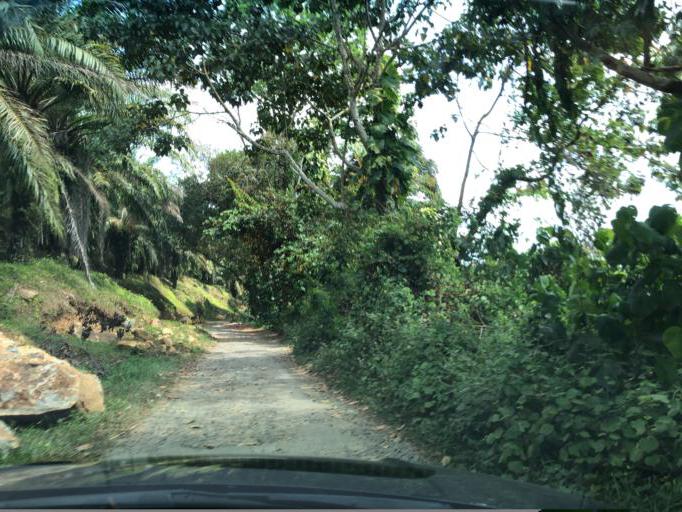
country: LK
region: Western
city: Horawala Junction
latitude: 6.5453
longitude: 80.0946
